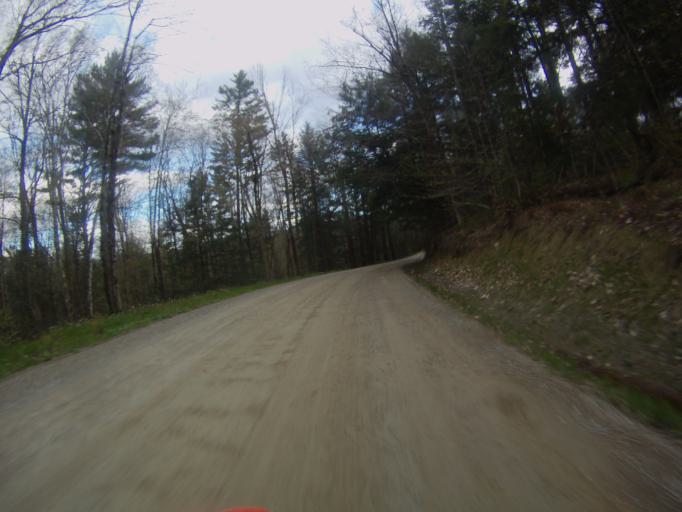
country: US
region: Vermont
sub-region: Addison County
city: Middlebury (village)
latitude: 43.9845
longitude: -73.0527
